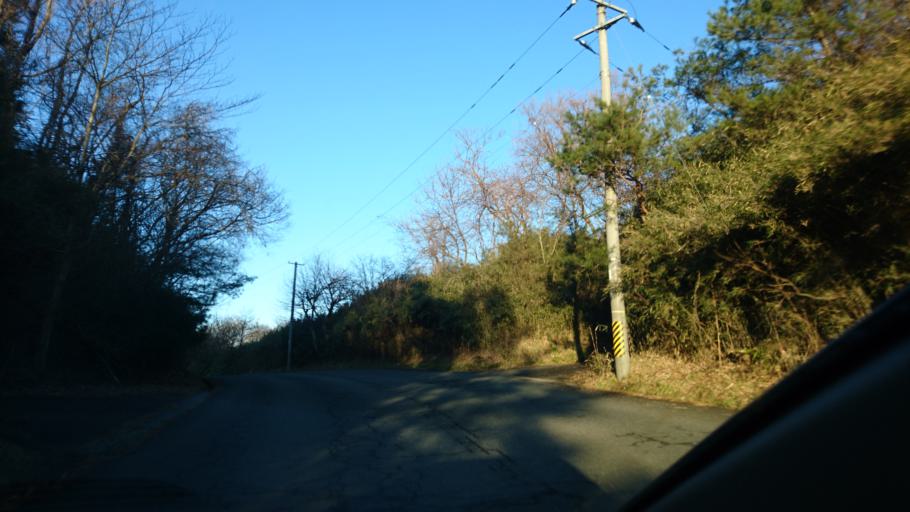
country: JP
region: Miyagi
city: Furukawa
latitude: 38.6749
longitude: 140.9155
